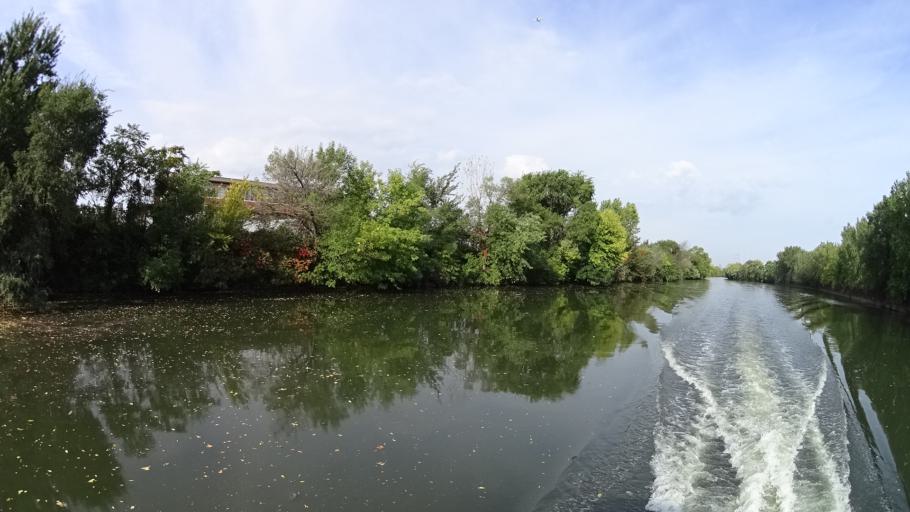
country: US
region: Illinois
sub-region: Cook County
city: Chicago
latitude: 41.8325
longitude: -87.6586
